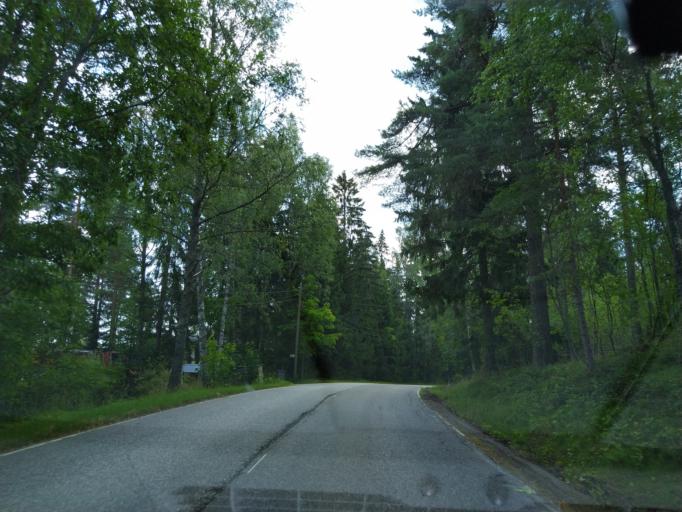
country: FI
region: Uusimaa
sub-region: Helsinki
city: Kirkkonummi
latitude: 60.0965
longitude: 24.4989
